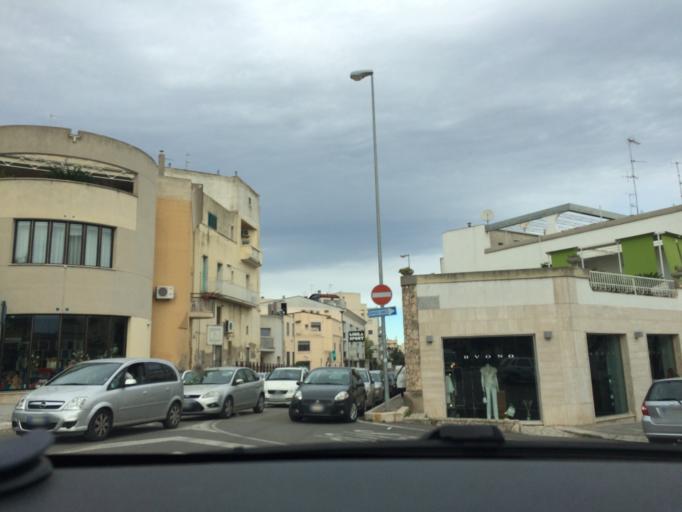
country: IT
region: Basilicate
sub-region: Provincia di Matera
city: Matera
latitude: 40.6705
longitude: 16.6060
